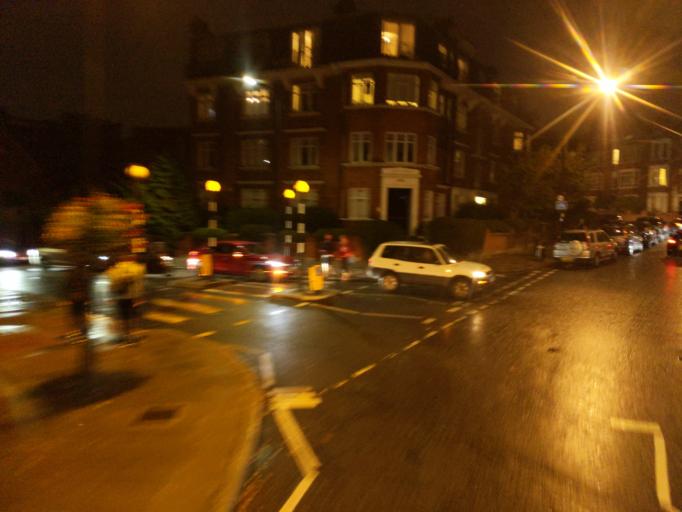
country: GB
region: England
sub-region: Greater London
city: Belsize Park
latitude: 51.5521
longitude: -0.1929
